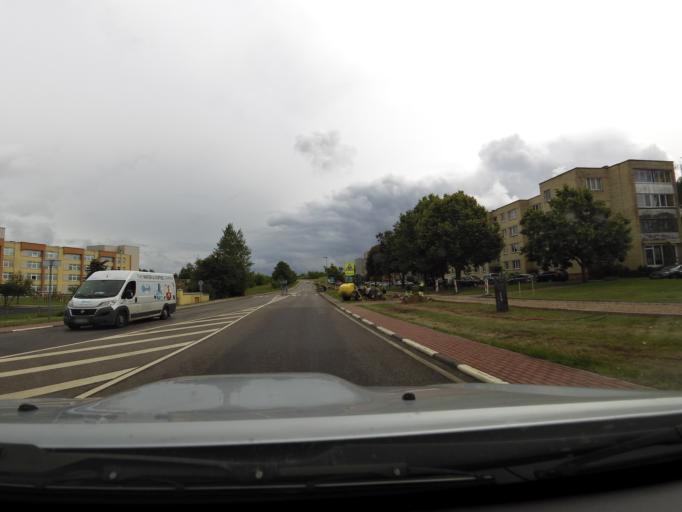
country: LT
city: Moletai
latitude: 55.2258
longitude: 25.4079
